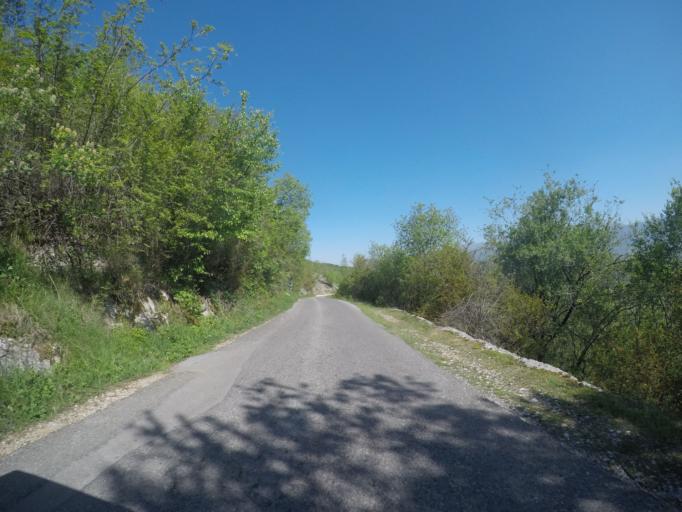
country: ME
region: Danilovgrad
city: Danilovgrad
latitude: 42.5192
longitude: 19.0962
